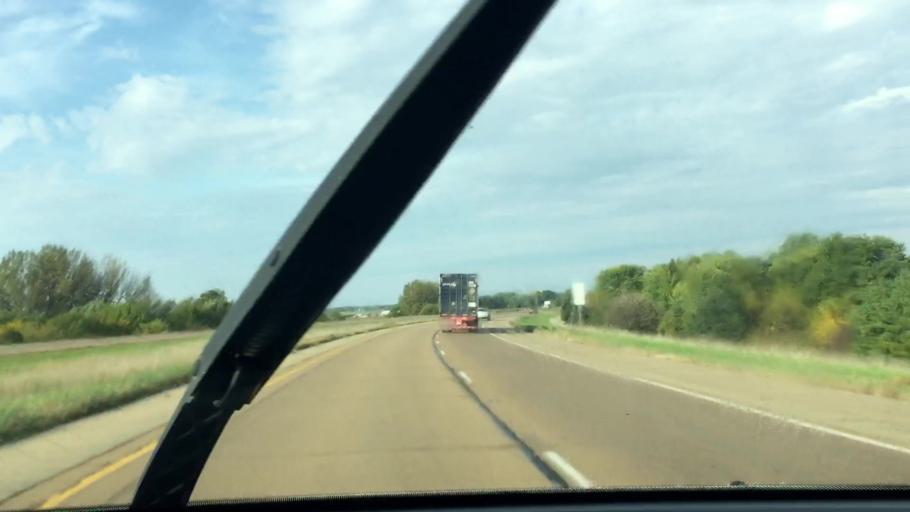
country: US
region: Illinois
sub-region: Whiteside County
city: Rock Falls
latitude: 41.7521
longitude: -89.6463
